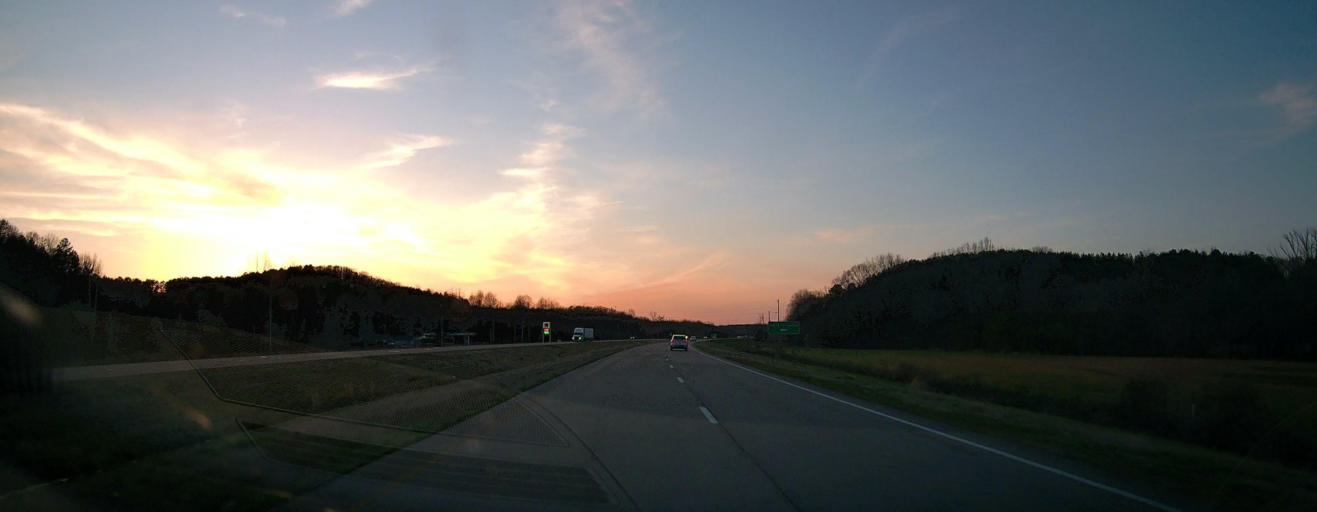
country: US
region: Mississippi
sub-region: Alcorn County
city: Corinth
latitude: 34.9345
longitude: -88.7710
